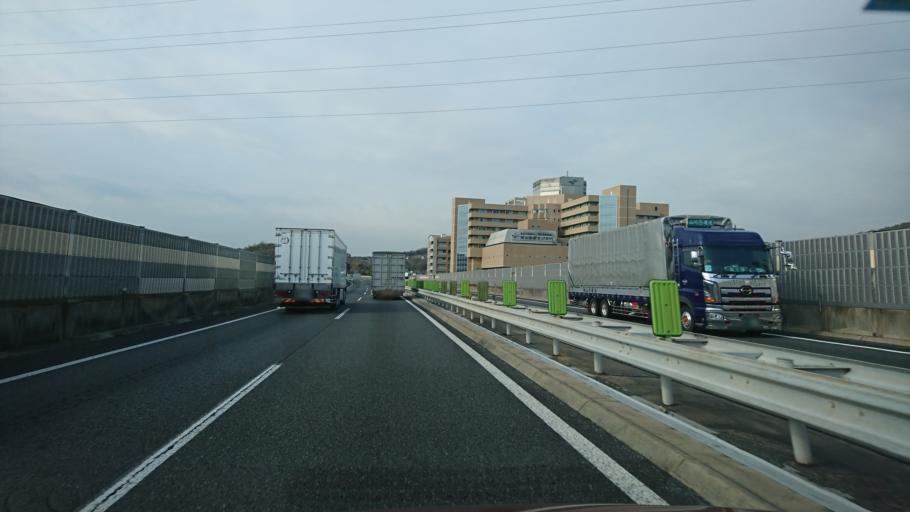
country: JP
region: Okayama
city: Okayama-shi
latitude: 34.7080
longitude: 133.9024
